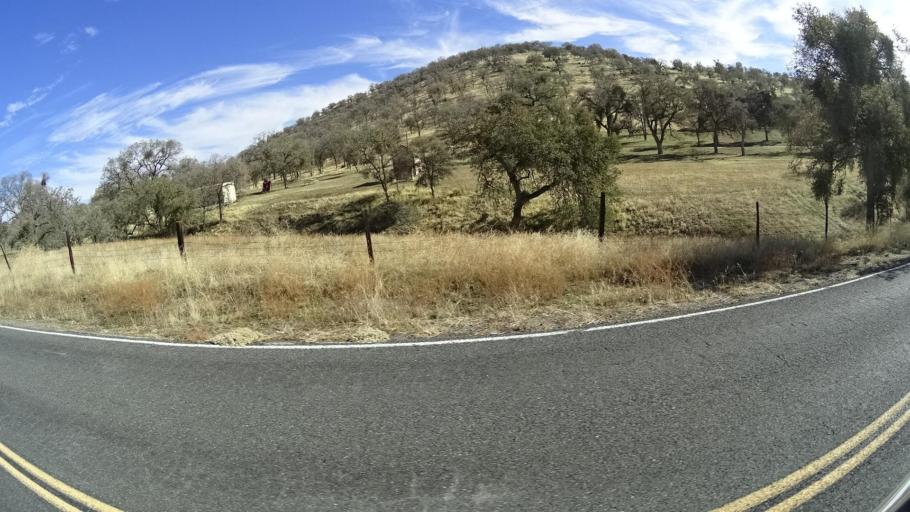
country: US
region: California
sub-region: Kern County
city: Alta Sierra
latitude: 35.6408
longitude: -118.7998
